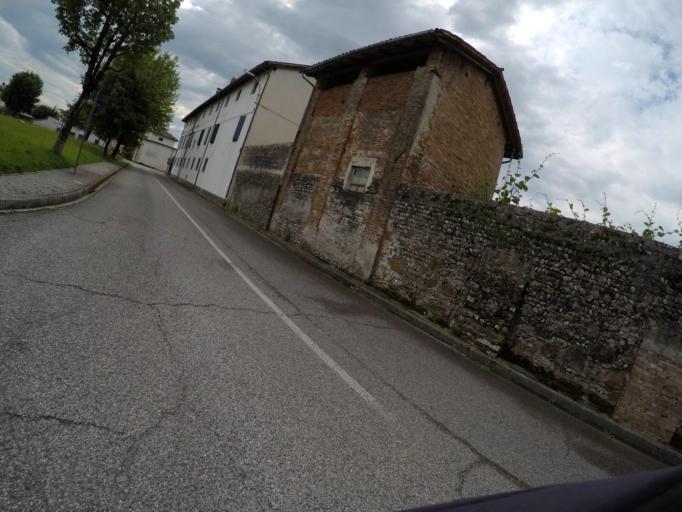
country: IT
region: Friuli Venezia Giulia
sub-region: Provincia di Udine
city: Pavia di Udine
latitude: 45.9974
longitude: 13.3059
